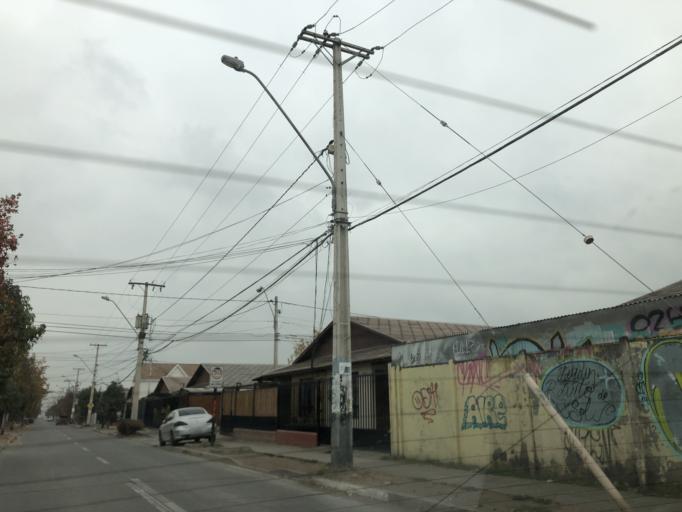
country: CL
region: Santiago Metropolitan
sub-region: Provincia de Santiago
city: La Pintana
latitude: -33.5772
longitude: -70.6043
